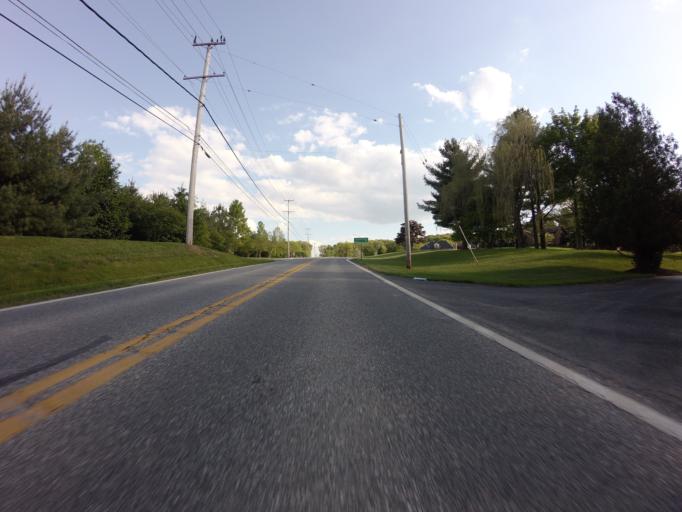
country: US
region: Maryland
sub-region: Baltimore County
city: Cockeysville
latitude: 39.4887
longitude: -76.7078
